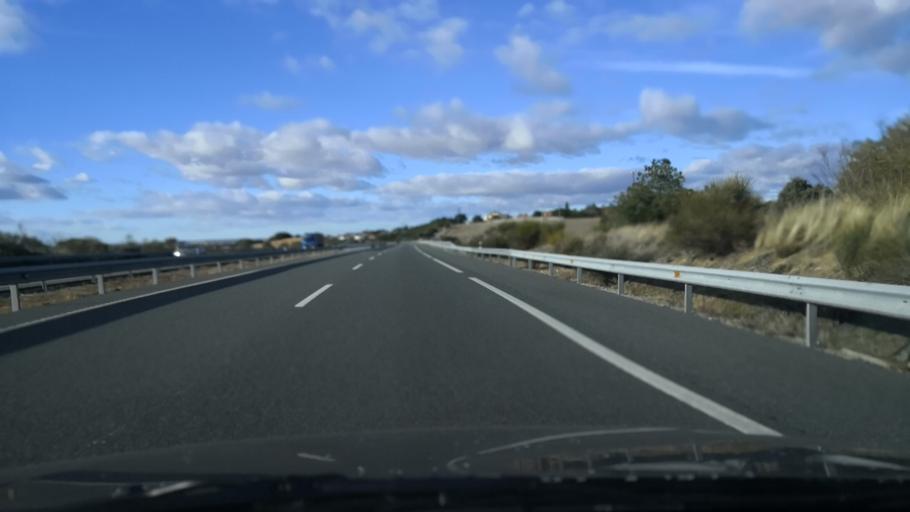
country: ES
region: Castille and Leon
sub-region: Provincia de Segovia
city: Labajos
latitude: 40.8501
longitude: -4.5437
